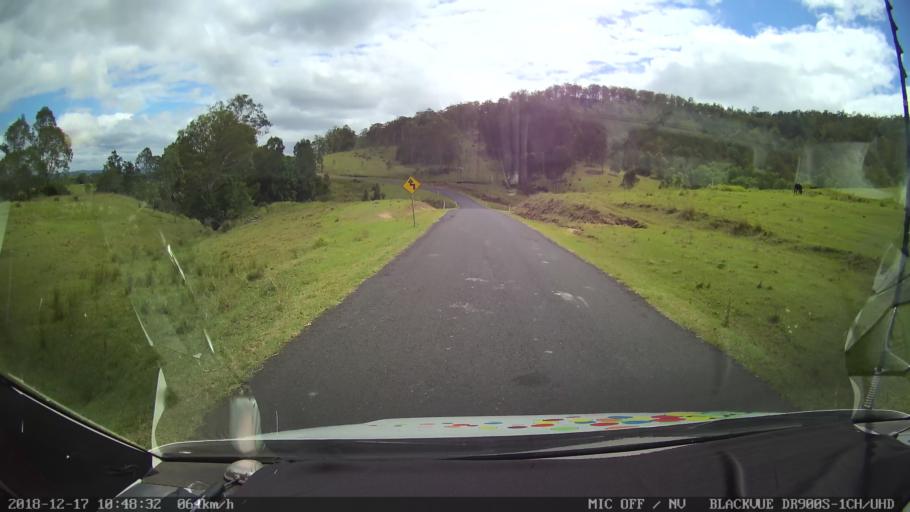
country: AU
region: New South Wales
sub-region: Clarence Valley
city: Gordon
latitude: -28.8722
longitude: 152.5712
